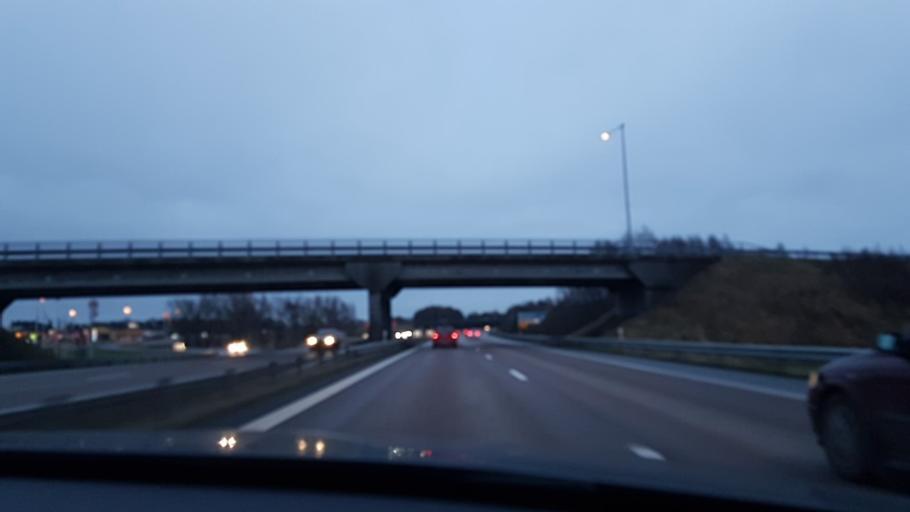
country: SE
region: Skane
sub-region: Kavlinge Kommun
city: Hofterup
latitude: 55.7685
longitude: 12.9835
